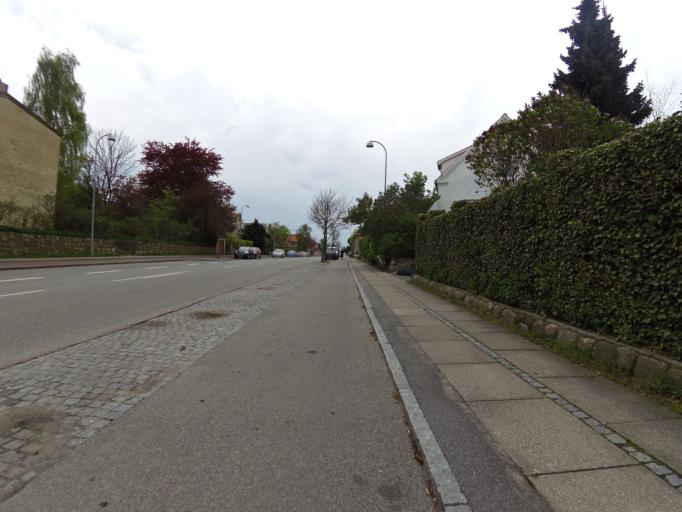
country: DK
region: Capital Region
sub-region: Gladsaxe Municipality
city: Buddinge
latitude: 55.7417
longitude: 12.5131
